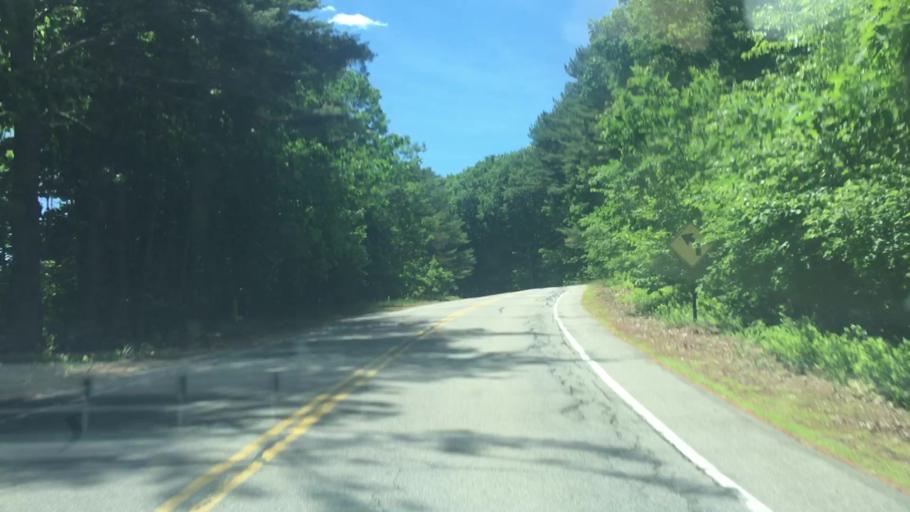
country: US
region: Maine
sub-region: York County
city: Kennebunk
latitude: 43.3742
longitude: -70.5274
